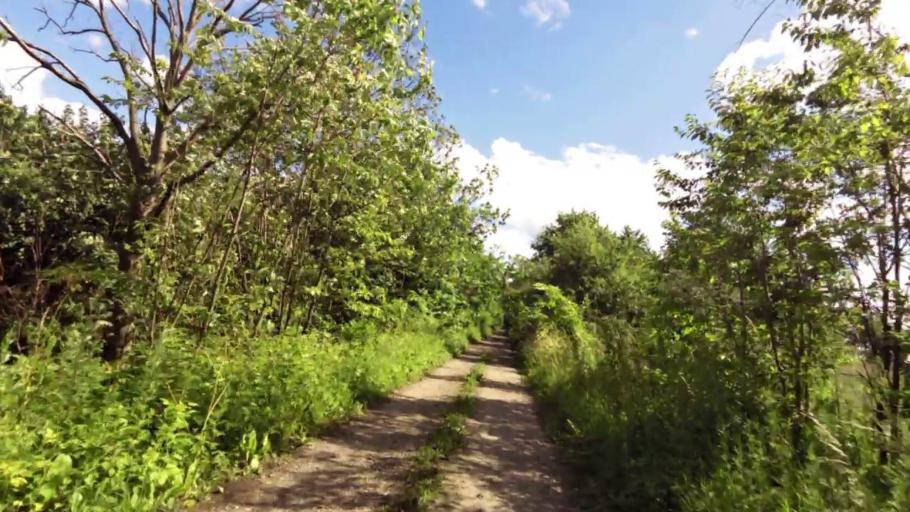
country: PL
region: West Pomeranian Voivodeship
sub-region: Powiat slawienski
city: Slawno
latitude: 54.5021
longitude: 16.7049
